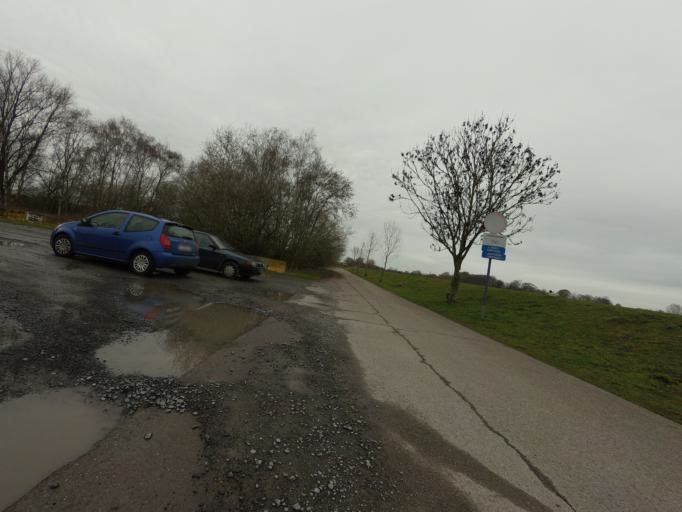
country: BE
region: Flanders
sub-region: Provincie Antwerpen
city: Lier
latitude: 51.1143
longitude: 4.5493
